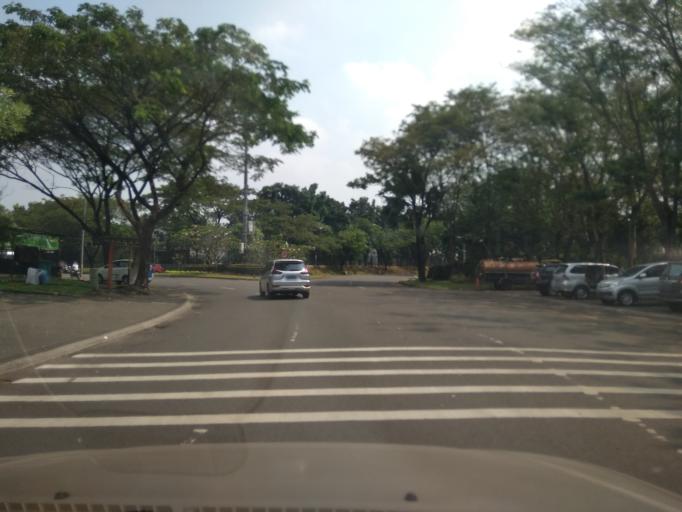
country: ID
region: West Java
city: Serpong
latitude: -6.3145
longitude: 106.6457
